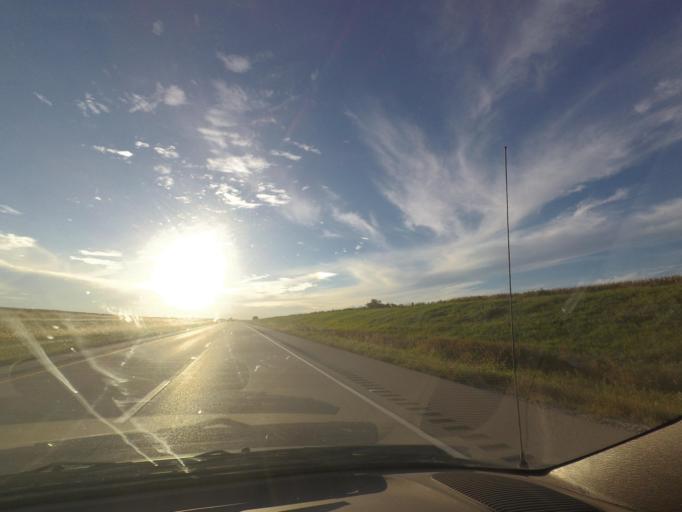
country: US
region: Illinois
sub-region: Morgan County
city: Jacksonville
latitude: 39.7386
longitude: -90.0924
